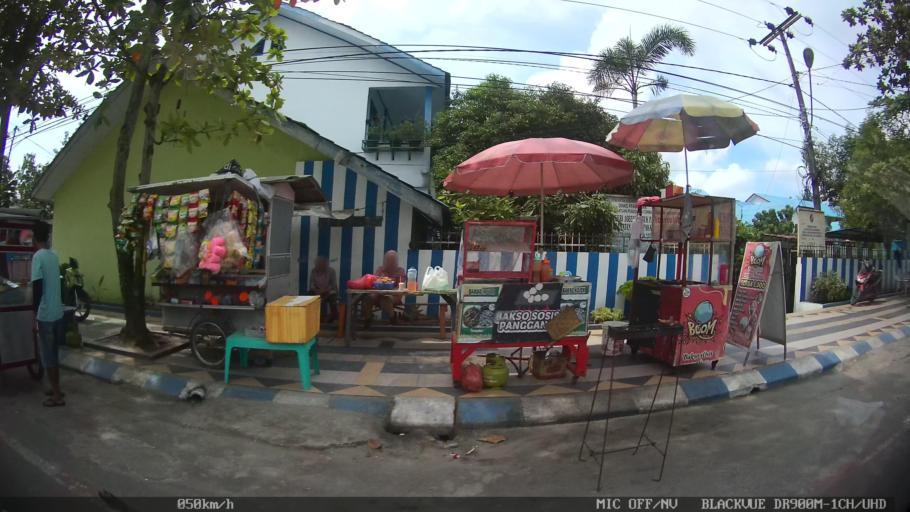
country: ID
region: North Sumatra
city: Percut
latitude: 3.5592
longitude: 98.8694
